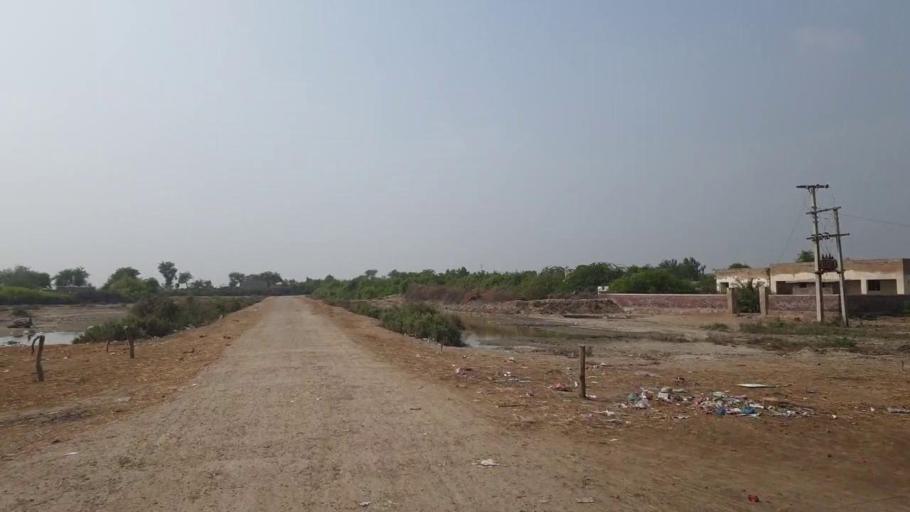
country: PK
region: Sindh
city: Kario
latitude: 24.8787
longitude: 68.5129
